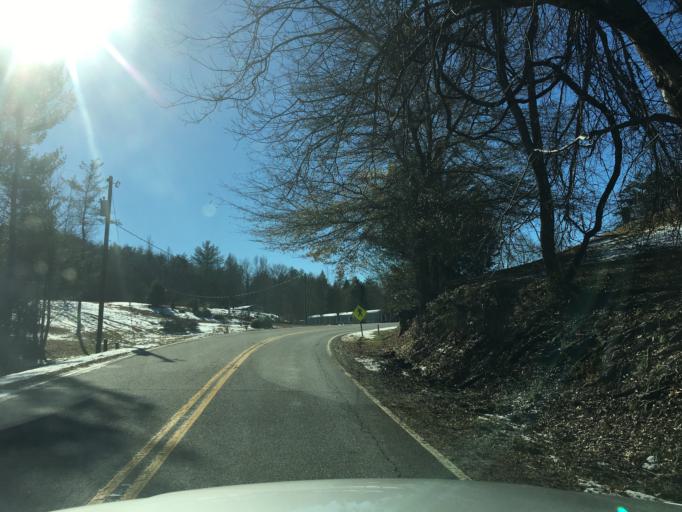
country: US
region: South Carolina
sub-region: Greenville County
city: Slater-Marietta
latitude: 35.0708
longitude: -82.6151
